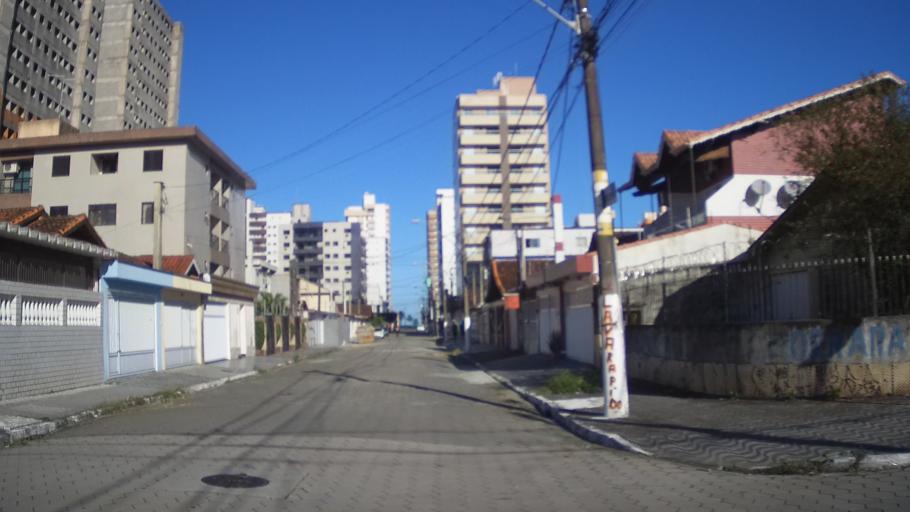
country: BR
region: Sao Paulo
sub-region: Praia Grande
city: Praia Grande
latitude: -24.0284
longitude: -46.4808
